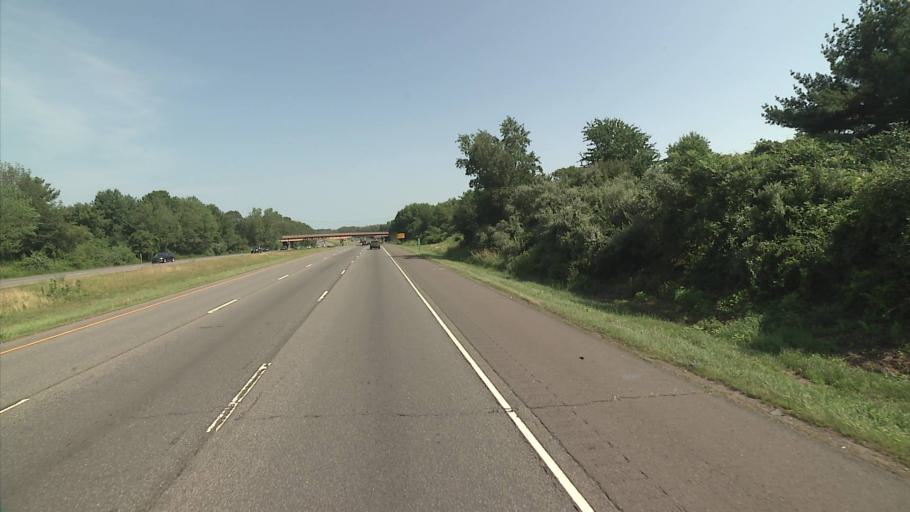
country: US
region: Connecticut
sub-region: New Haven County
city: Meriden
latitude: 41.5084
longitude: -72.7692
